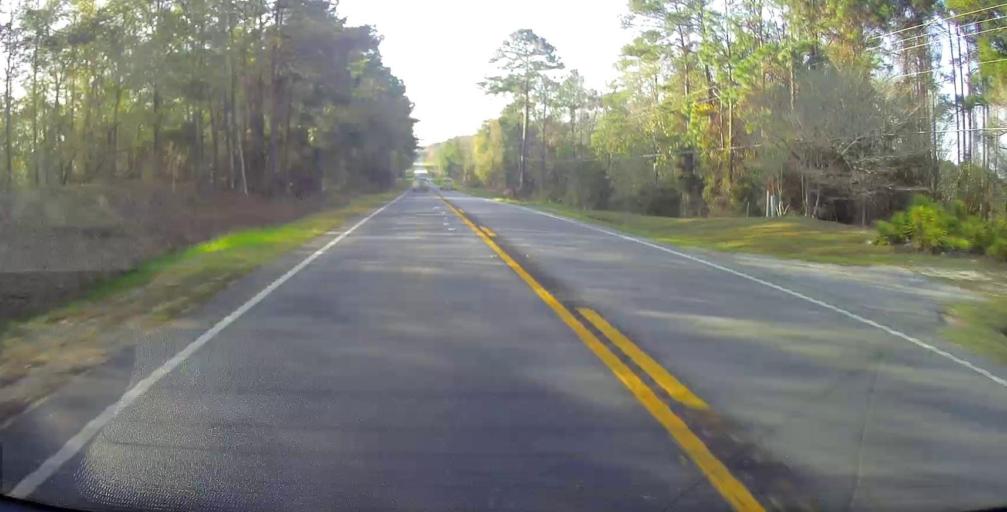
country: US
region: Georgia
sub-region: Tattnall County
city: Reidsville
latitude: 32.0872
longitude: -82.1429
